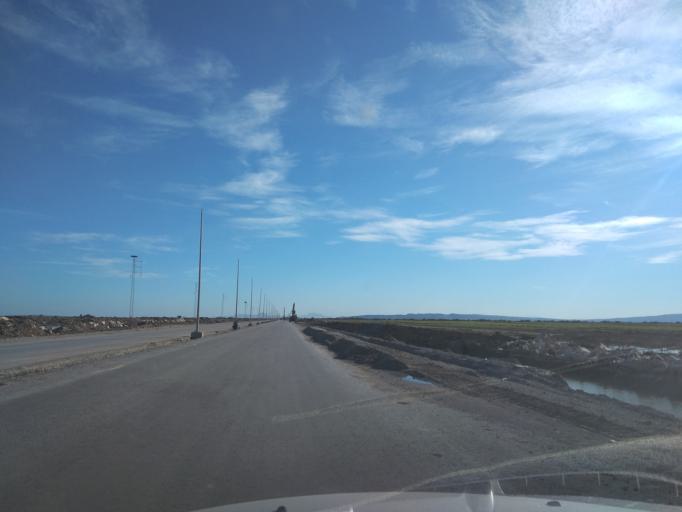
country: TN
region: Ariana
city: Qal'at al Andalus
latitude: 37.0330
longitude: 10.1353
